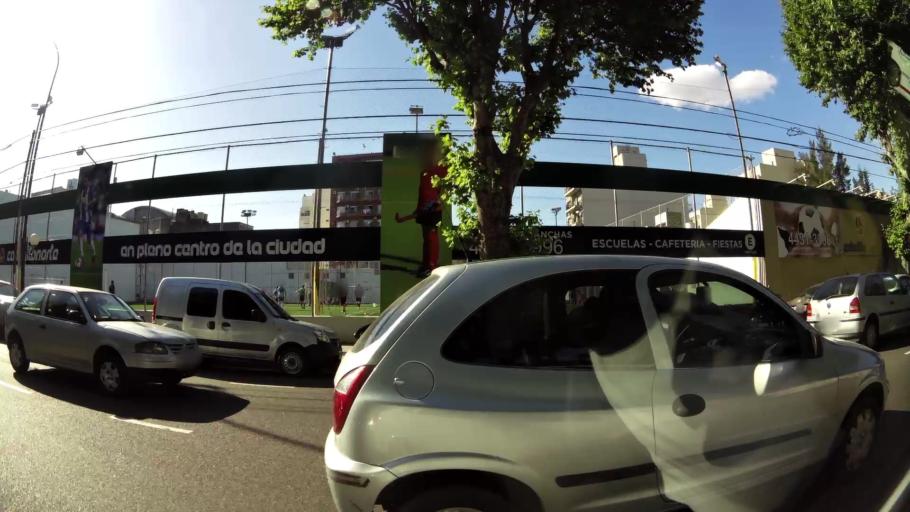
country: AR
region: Buenos Aires F.D.
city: Villa Santa Rita
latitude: -34.6196
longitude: -58.4519
